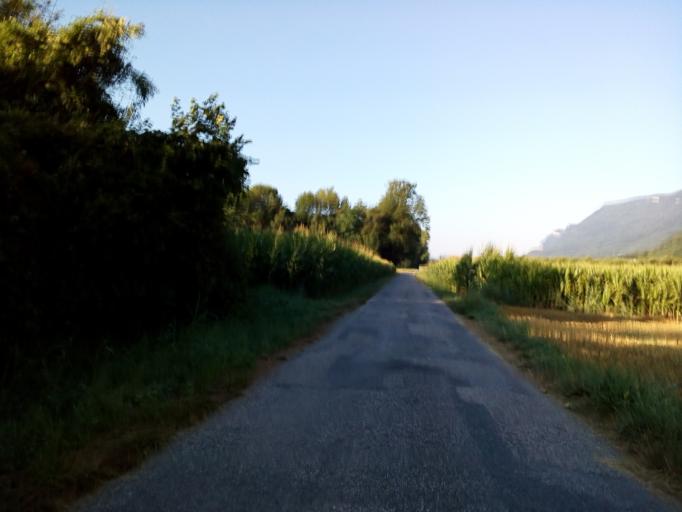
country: FR
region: Rhone-Alpes
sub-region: Departement de l'Isere
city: Le Cheylas
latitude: 45.3918
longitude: 5.9783
